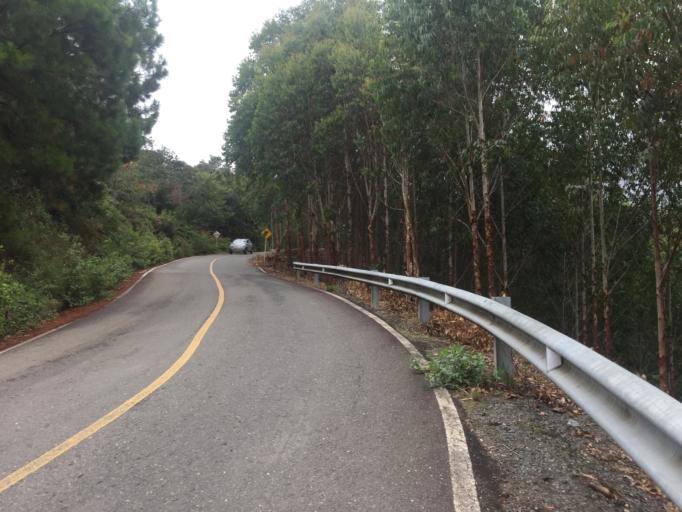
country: CO
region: Valle del Cauca
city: Dagua
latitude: 3.7044
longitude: -76.5868
